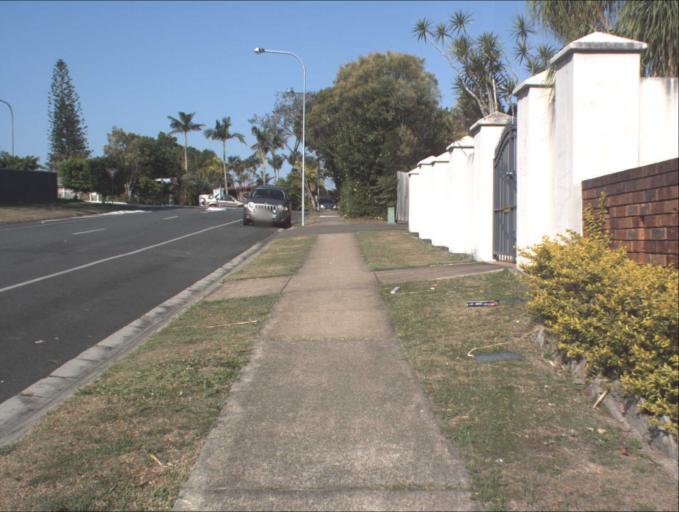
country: AU
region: Queensland
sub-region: Logan
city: Beenleigh
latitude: -27.6978
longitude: 153.1812
